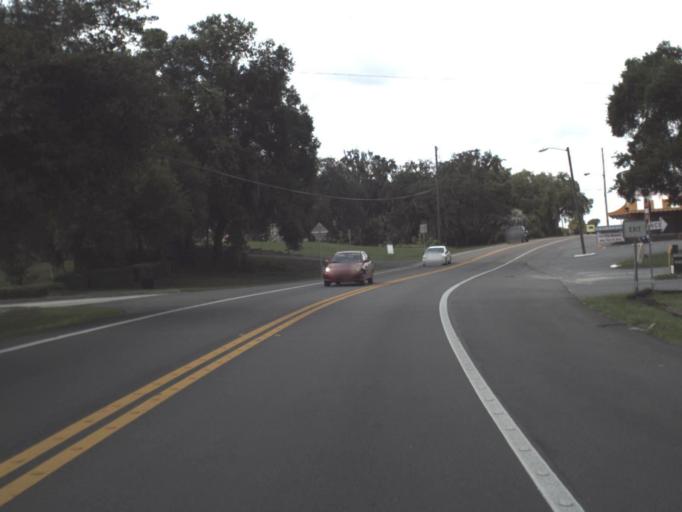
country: US
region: Florida
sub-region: Citrus County
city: Floral City
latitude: 28.7515
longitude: -82.2970
